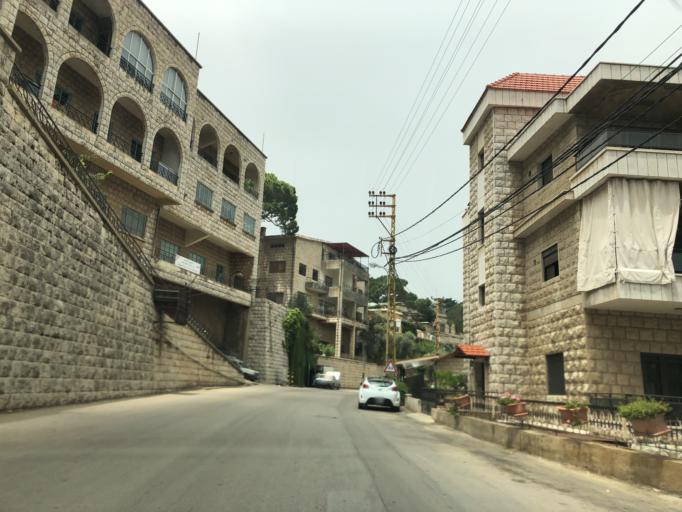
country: LB
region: Mont-Liban
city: Jdaidet el Matn
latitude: 33.8787
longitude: 35.6245
